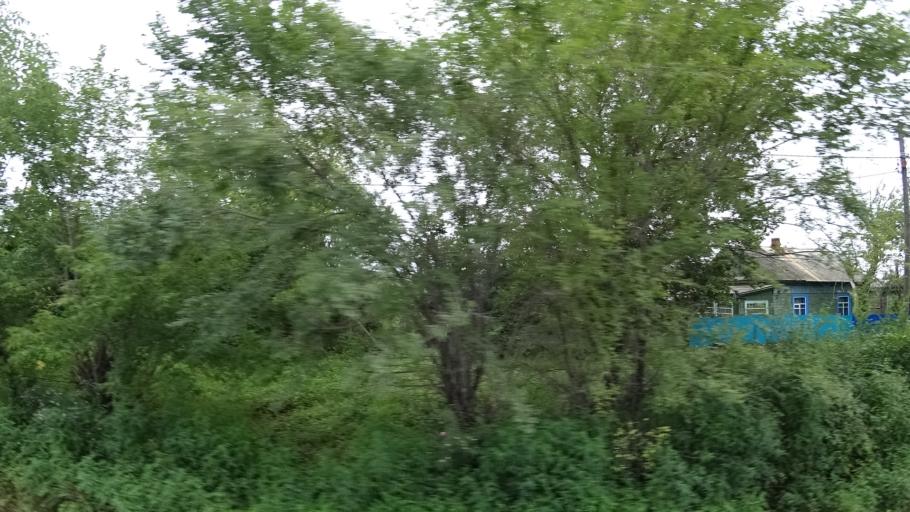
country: RU
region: Primorskiy
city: Chernigovka
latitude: 44.3456
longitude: 132.5611
